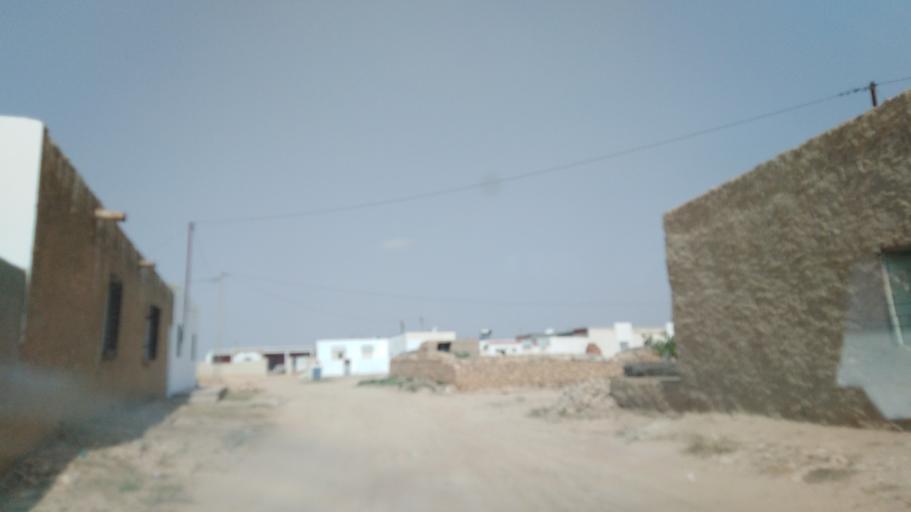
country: TN
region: Safaqis
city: Sfax
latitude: 34.6270
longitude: 10.5737
